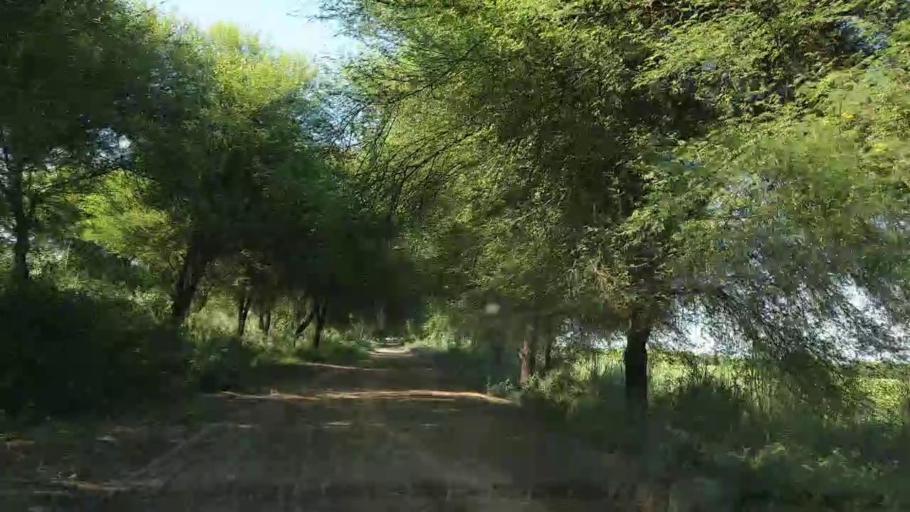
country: PK
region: Sindh
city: Tando Jam
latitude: 25.3561
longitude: 68.5699
